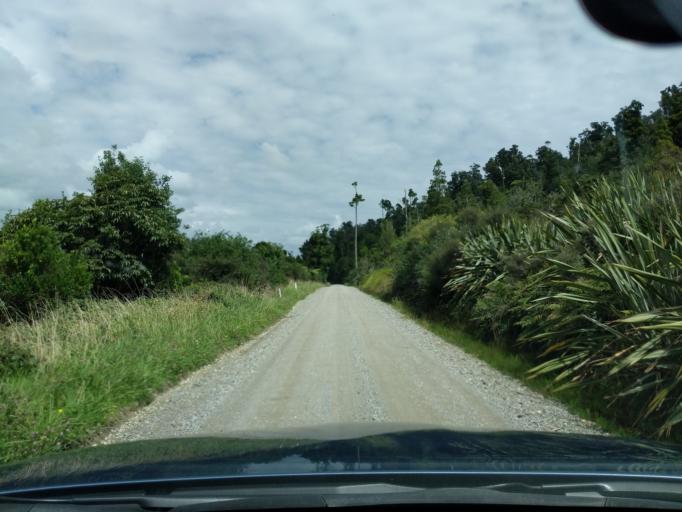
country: NZ
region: Tasman
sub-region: Tasman District
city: Takaka
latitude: -40.6465
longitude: 172.4721
